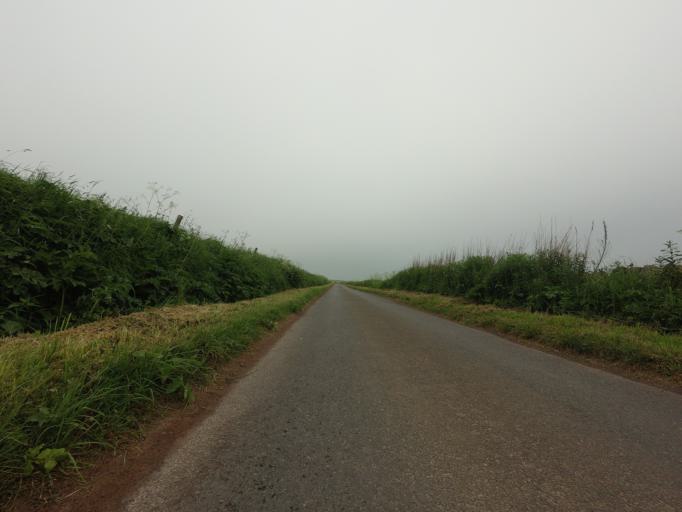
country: GB
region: Scotland
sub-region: Perth and Kinross
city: Abernethy
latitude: 56.2662
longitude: -3.3004
